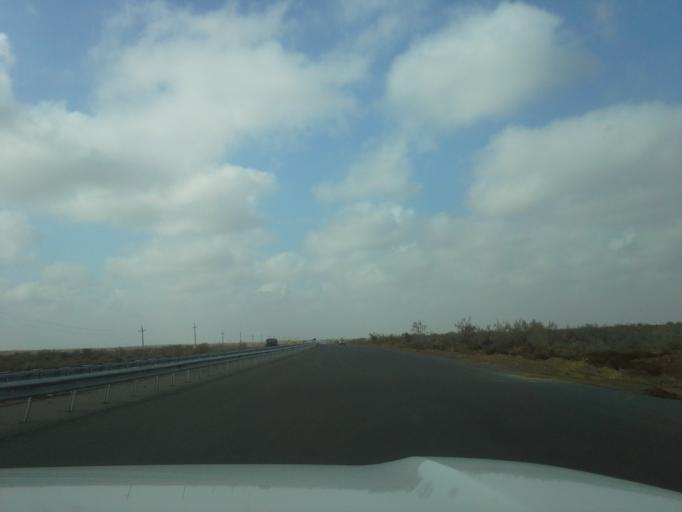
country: TM
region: Mary
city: Mary
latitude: 37.4140
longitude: 61.5479
